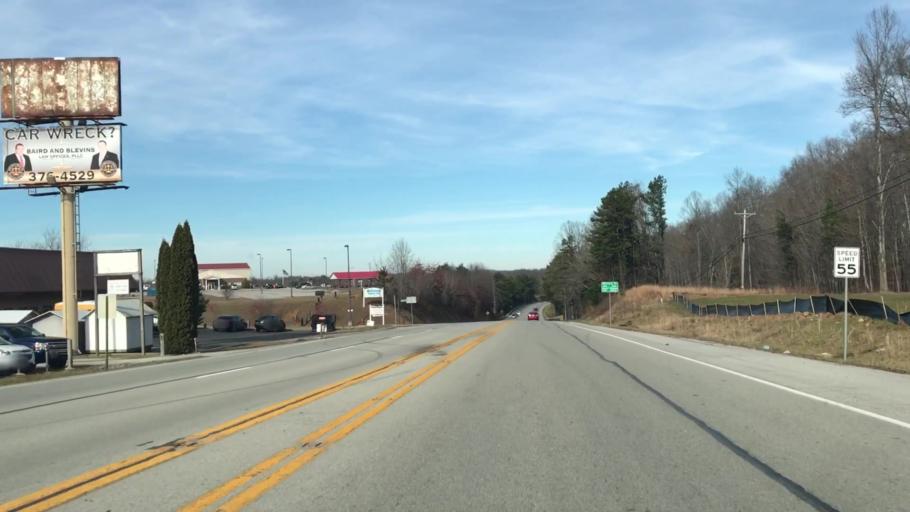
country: US
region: Kentucky
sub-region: McCreary County
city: Whitley City
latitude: 36.7497
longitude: -84.4745
